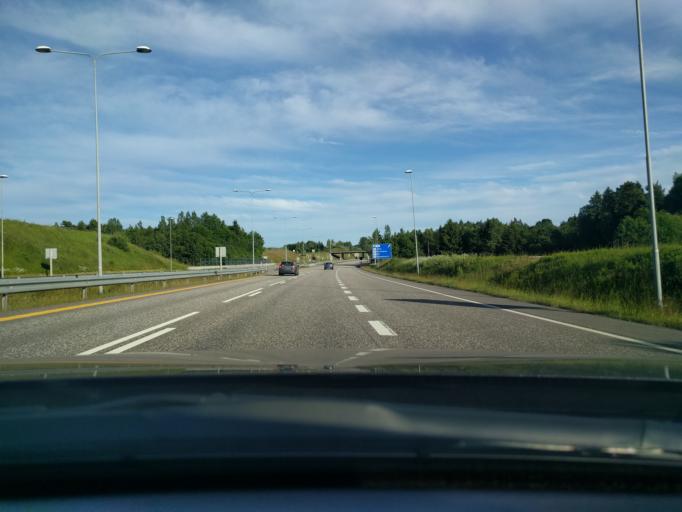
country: NO
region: Vestfold
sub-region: Holmestrand
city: Gullhaug
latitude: 59.5125
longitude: 10.2059
